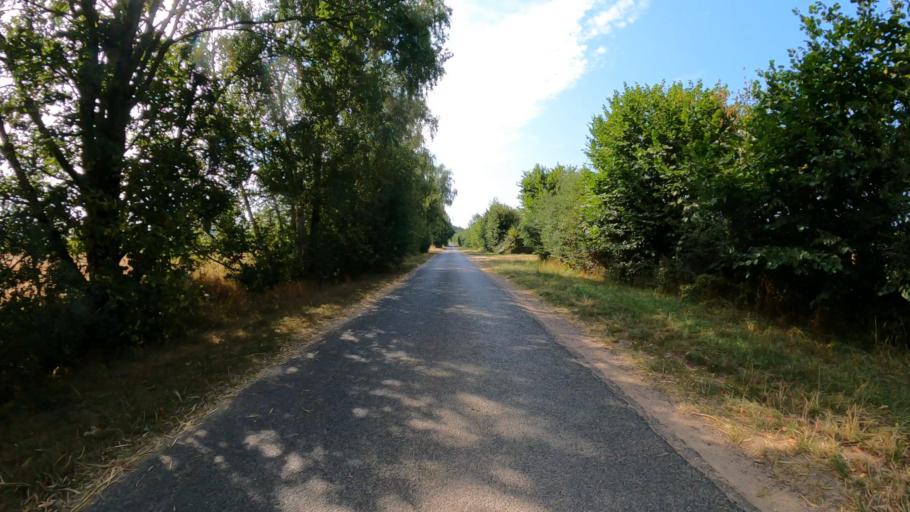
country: DE
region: Schleswig-Holstein
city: Hamwarde
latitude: 53.4453
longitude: 10.4198
